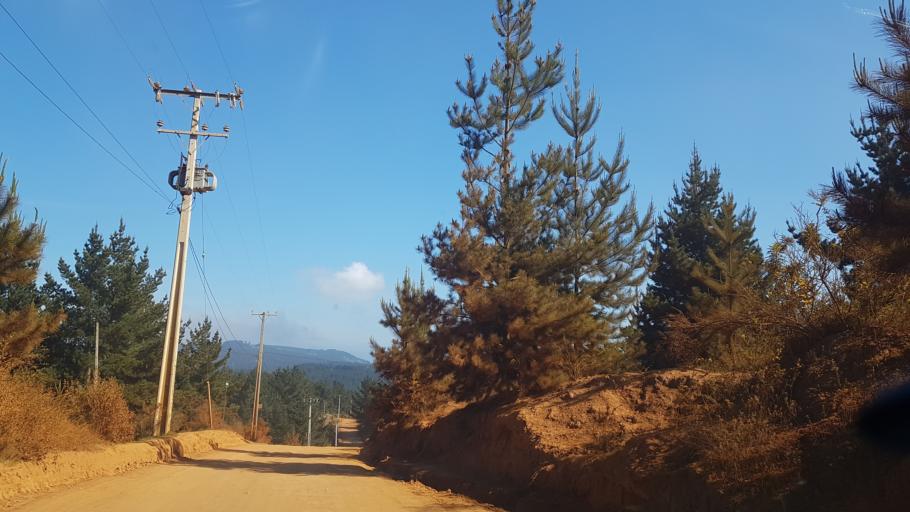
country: CL
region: Valparaiso
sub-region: Provincia de Valparaiso
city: Valparaiso
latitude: -33.1337
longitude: -71.6601
